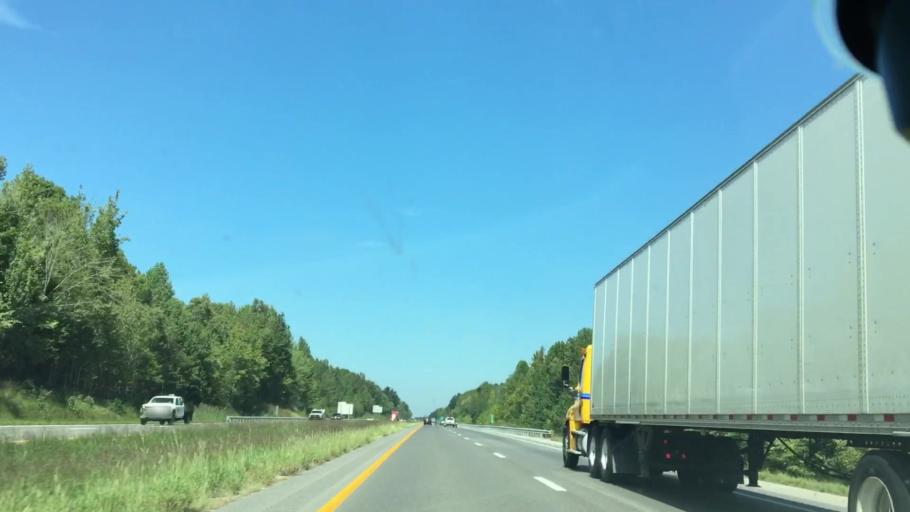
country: US
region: Kentucky
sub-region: Hopkins County
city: Earlington
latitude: 37.2670
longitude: -87.4535
